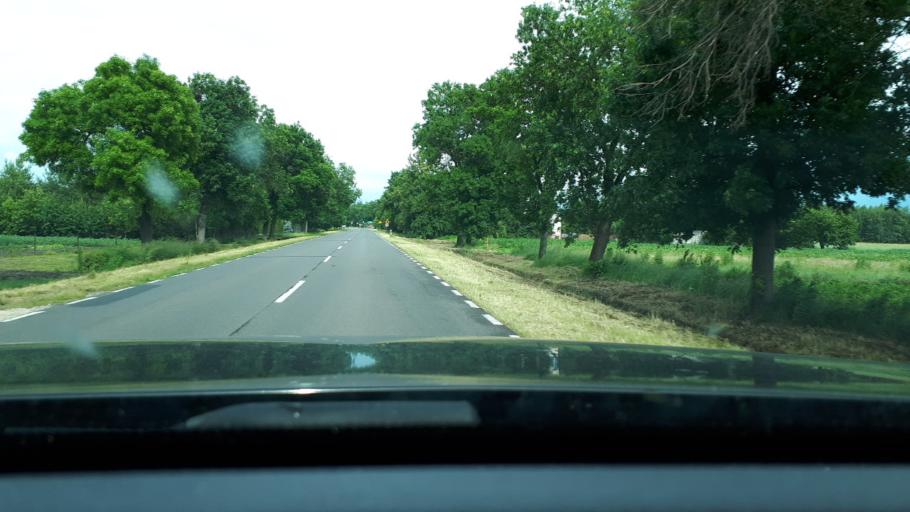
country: PL
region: Masovian Voivodeship
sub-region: Powiat sochaczewski
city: Paprotnia
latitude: 52.2657
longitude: 20.3769
